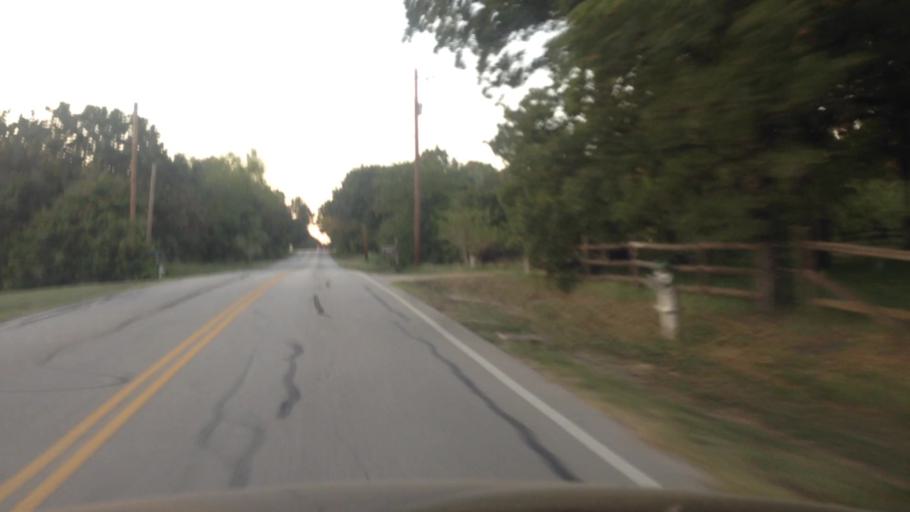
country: US
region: Texas
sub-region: Tarrant County
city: Keller
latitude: 32.9437
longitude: -97.2031
